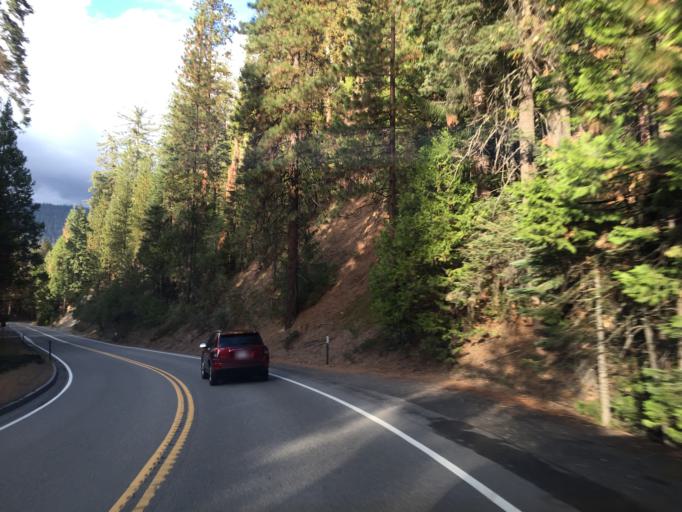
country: US
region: California
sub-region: Madera County
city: Ahwahnee
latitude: 37.5190
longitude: -119.6246
